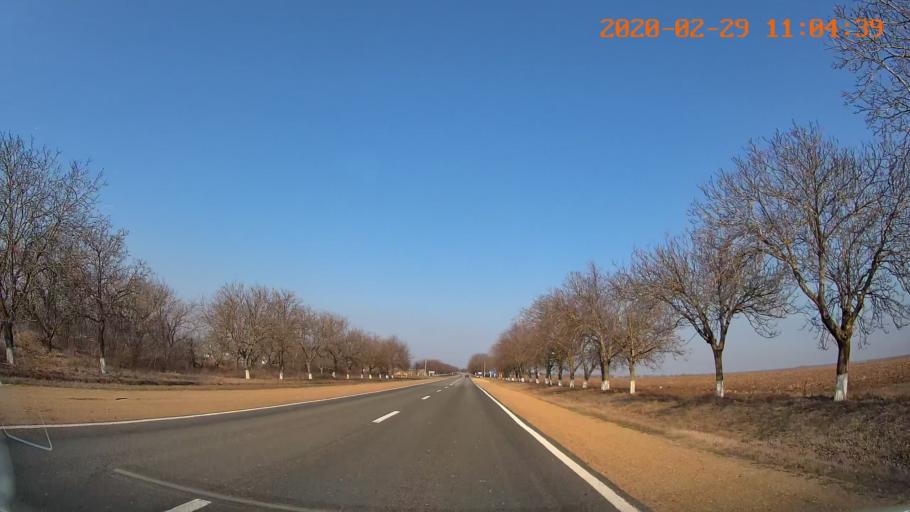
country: MD
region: Criuleni
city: Criuleni
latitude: 47.1920
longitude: 29.1997
